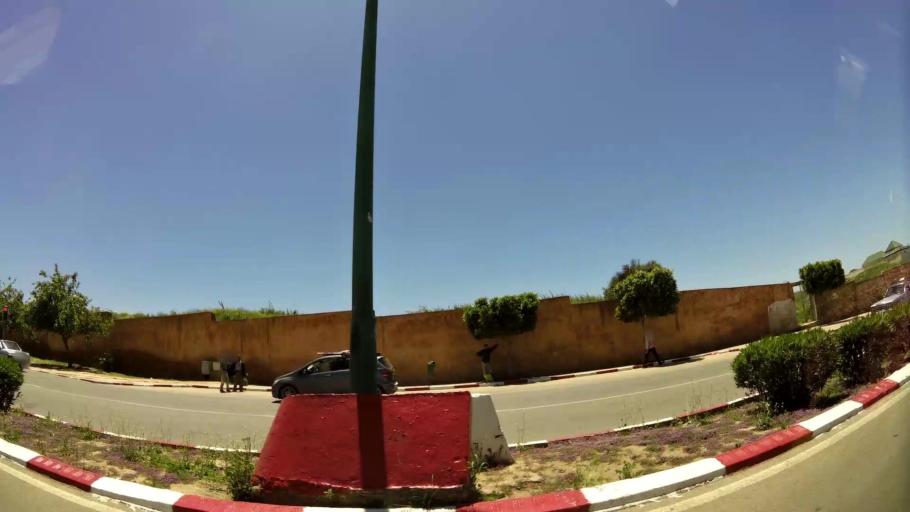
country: MA
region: Meknes-Tafilalet
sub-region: Meknes
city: Meknes
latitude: 33.9020
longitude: -5.5692
